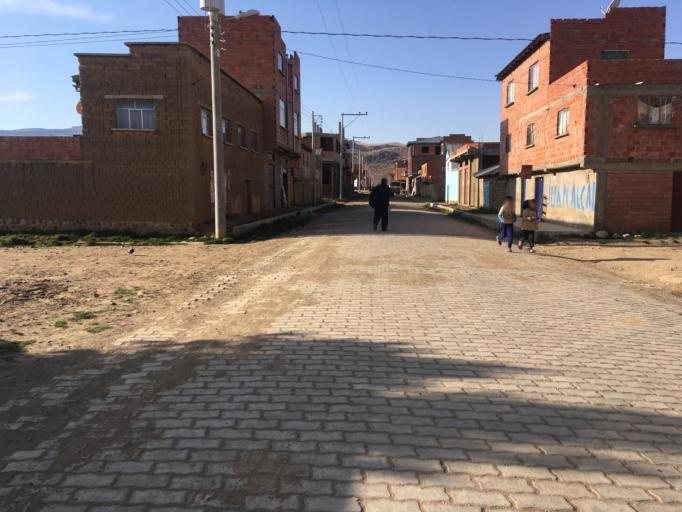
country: BO
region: La Paz
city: Huatajata
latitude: -16.1916
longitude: -68.7445
